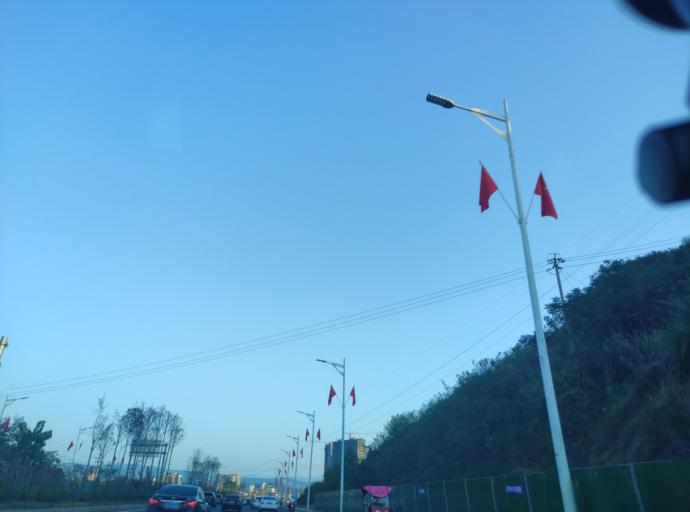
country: CN
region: Jiangxi Sheng
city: Pingxiang
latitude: 27.6428
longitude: 113.8266
